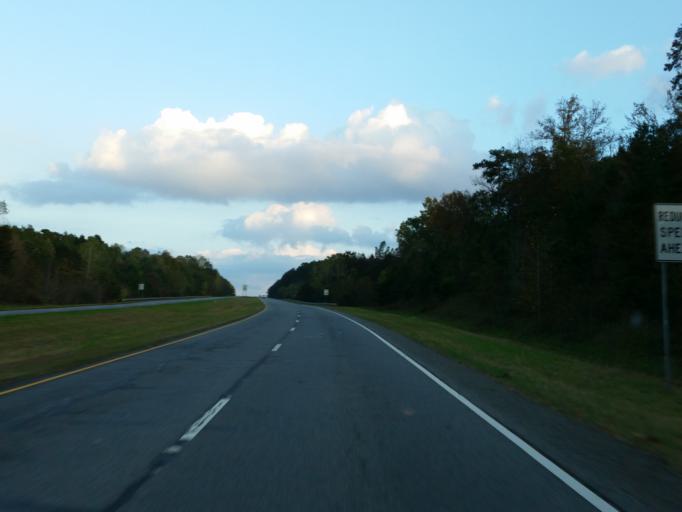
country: US
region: Georgia
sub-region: Houston County
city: Perry
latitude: 32.3950
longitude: -83.6369
